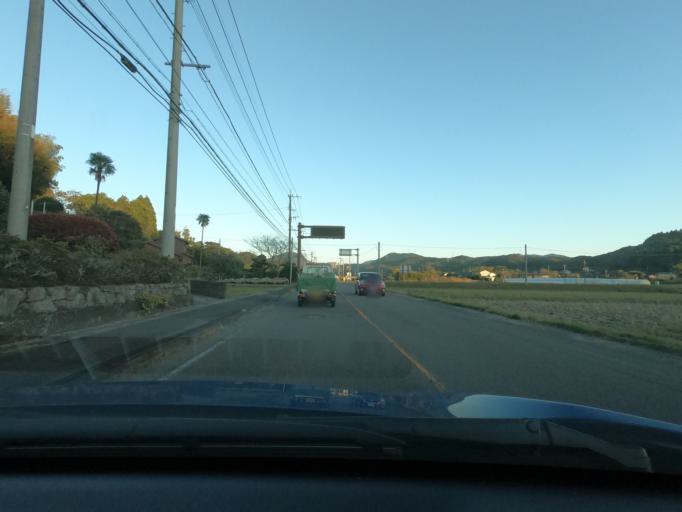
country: JP
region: Kagoshima
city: Satsumasendai
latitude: 31.7953
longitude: 130.4439
